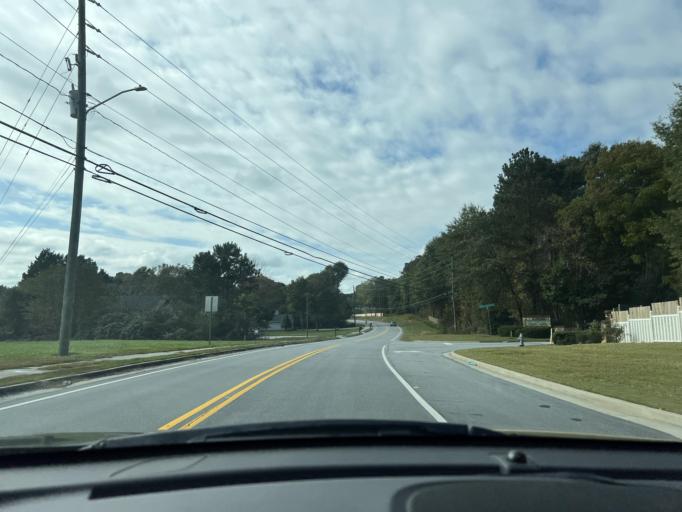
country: US
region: Georgia
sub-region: Gwinnett County
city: Grayson
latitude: 33.9009
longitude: -83.9488
